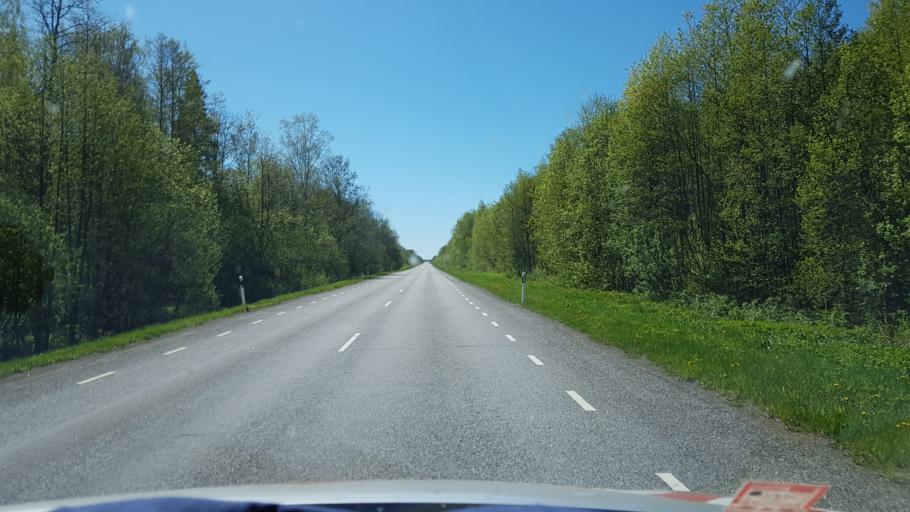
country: EE
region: Ida-Virumaa
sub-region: Narva-Joesuu linn
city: Narva-Joesuu
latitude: 59.3406
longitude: 27.9855
